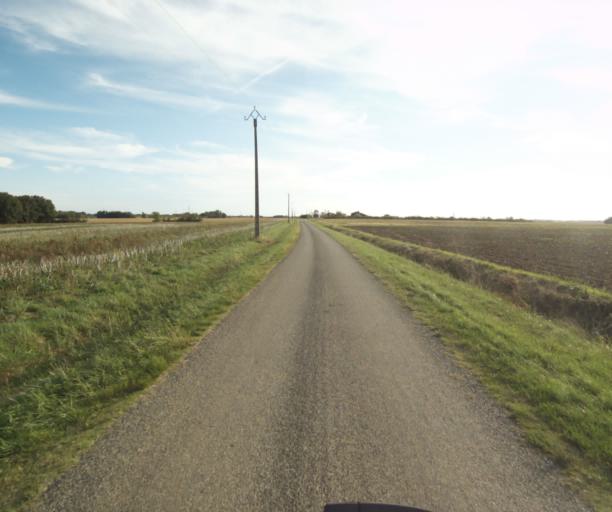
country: FR
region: Midi-Pyrenees
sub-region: Departement du Tarn-et-Garonne
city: Finhan
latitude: 43.9165
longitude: 1.1319
